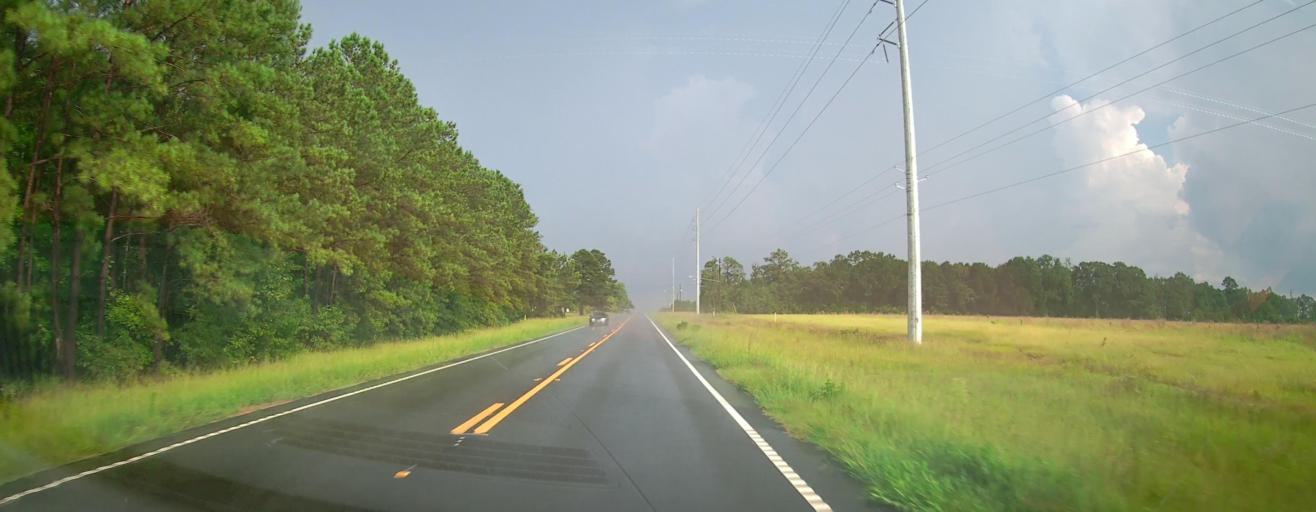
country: US
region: Georgia
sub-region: Twiggs County
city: Jeffersonville
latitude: 32.5965
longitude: -83.2344
